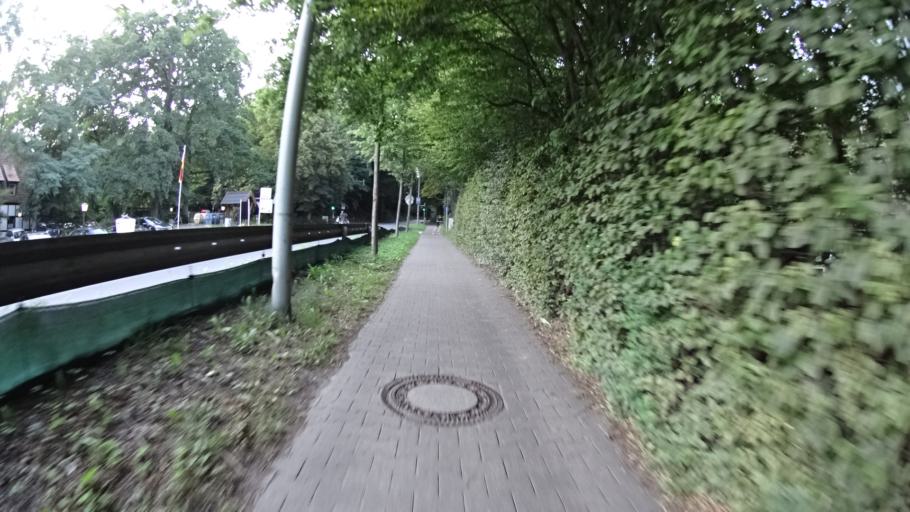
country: DE
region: Lower Saxony
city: Lueneburg
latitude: 53.2250
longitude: 10.3941
